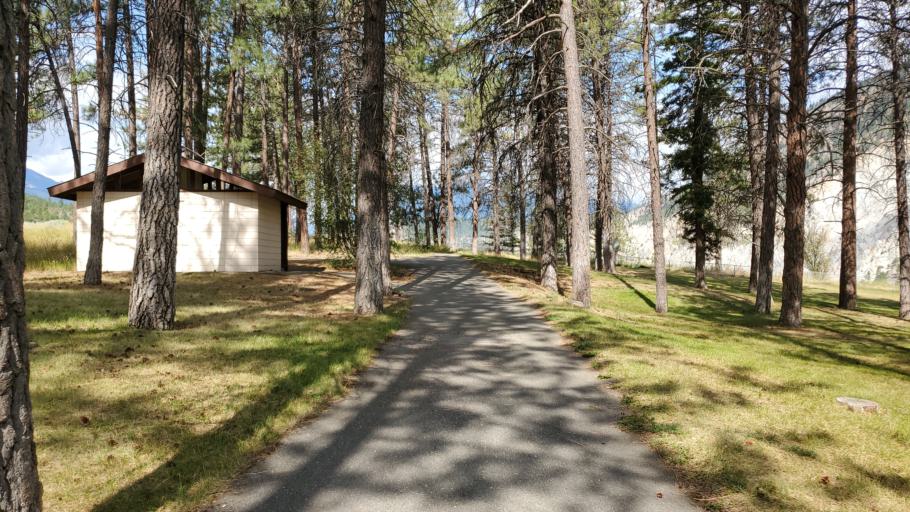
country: CA
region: British Columbia
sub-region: Thompson-Nicola Regional District
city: Ashcroft
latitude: 50.2549
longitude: -121.5105
